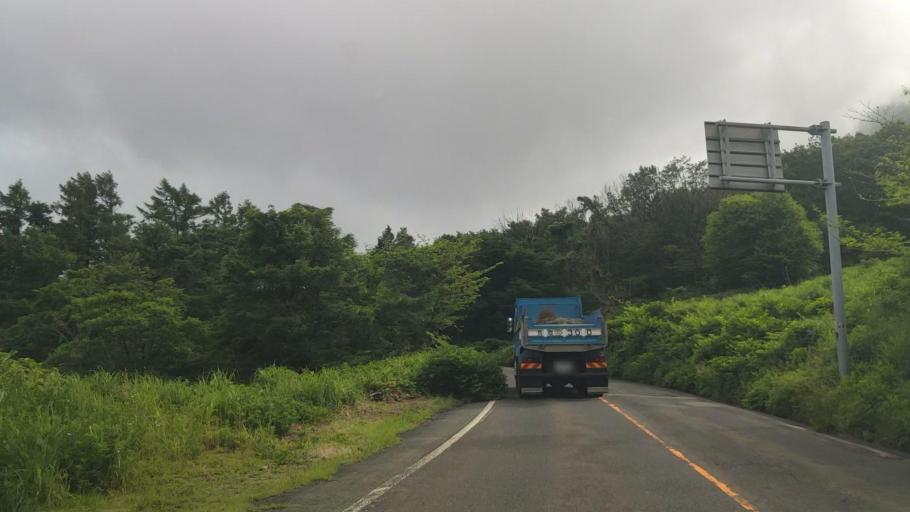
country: JP
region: Tottori
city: Yonago
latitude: 35.3709
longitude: 133.5164
